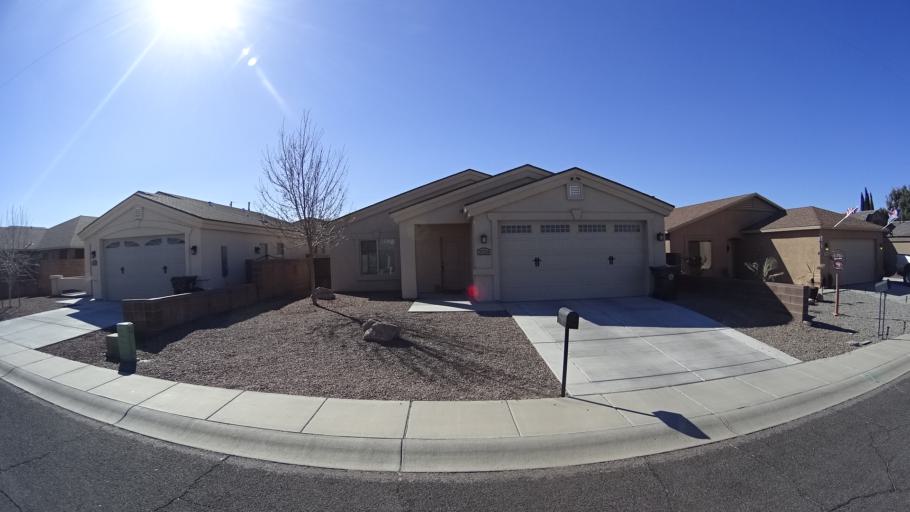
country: US
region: Arizona
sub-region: Mohave County
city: Kingman
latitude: 35.1965
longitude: -114.0150
